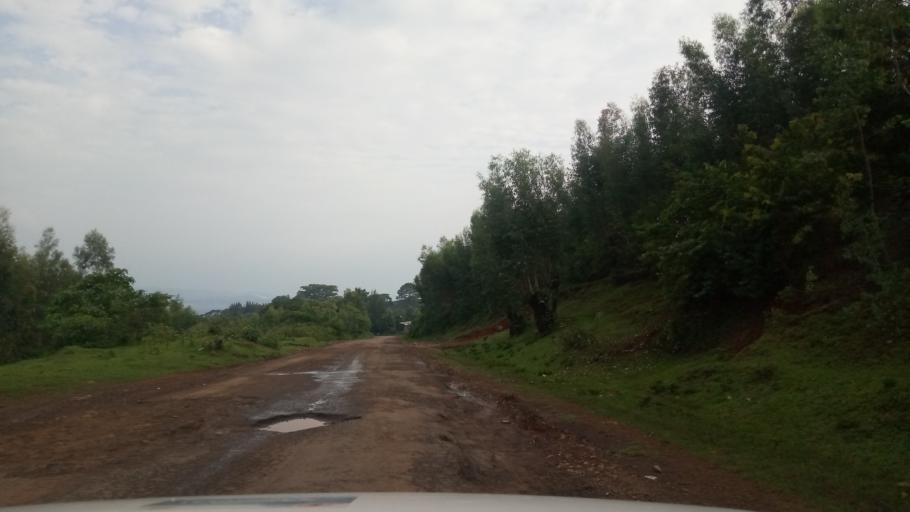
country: ET
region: Oromiya
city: Agaro
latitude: 7.7951
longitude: 36.7226
